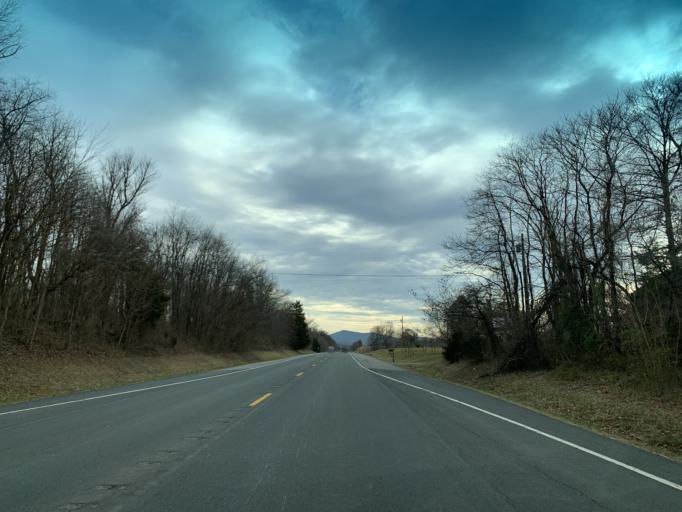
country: US
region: Maryland
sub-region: Washington County
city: Boonsboro
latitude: 39.4814
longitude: -77.6522
